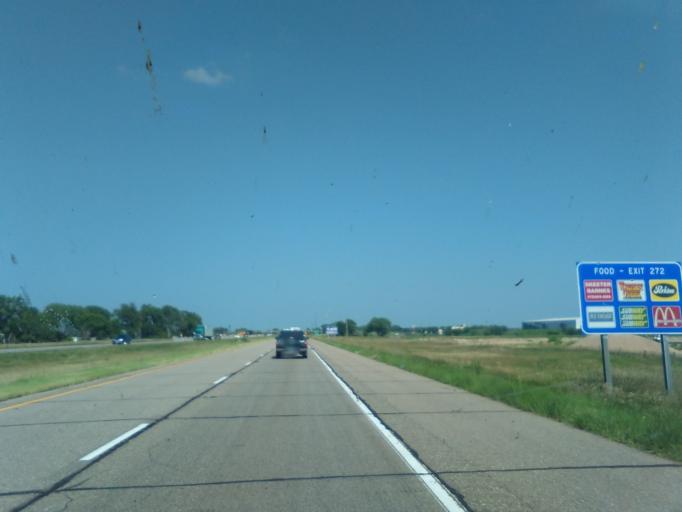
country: US
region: Nebraska
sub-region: Buffalo County
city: Kearney
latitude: 40.6700
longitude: -99.0999
